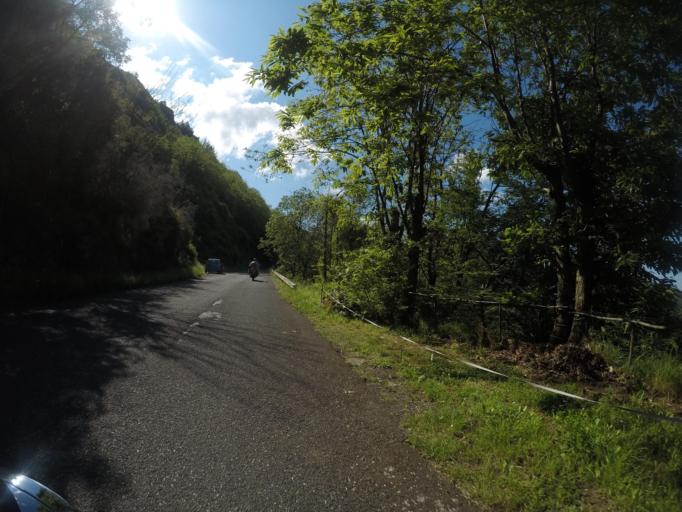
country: IT
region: Tuscany
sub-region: Provincia di Massa-Carrara
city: Montignoso
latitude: 44.0595
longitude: 10.1841
